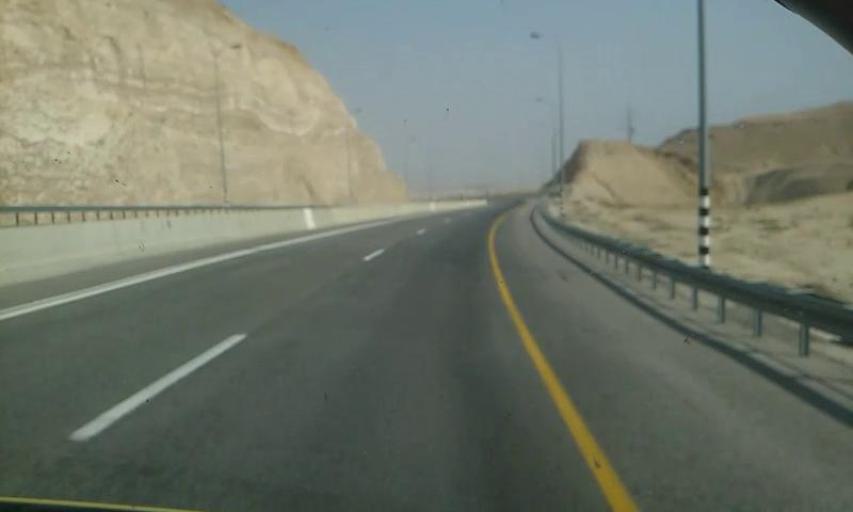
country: PS
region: West Bank
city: Jericho
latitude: 31.7997
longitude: 35.4412
